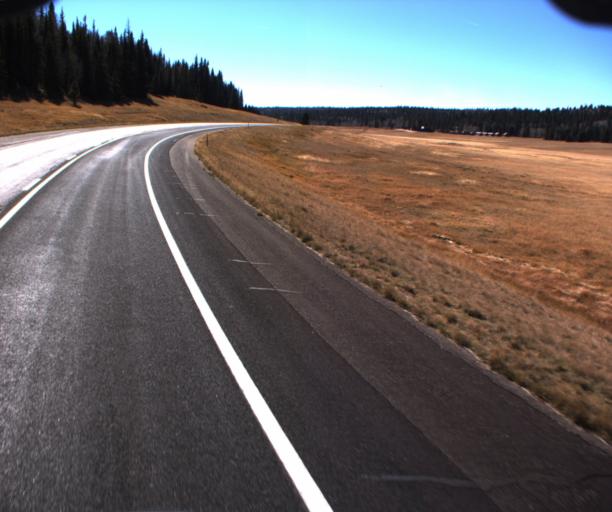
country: US
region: Arizona
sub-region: Coconino County
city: Grand Canyon
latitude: 36.4209
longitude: -112.1285
